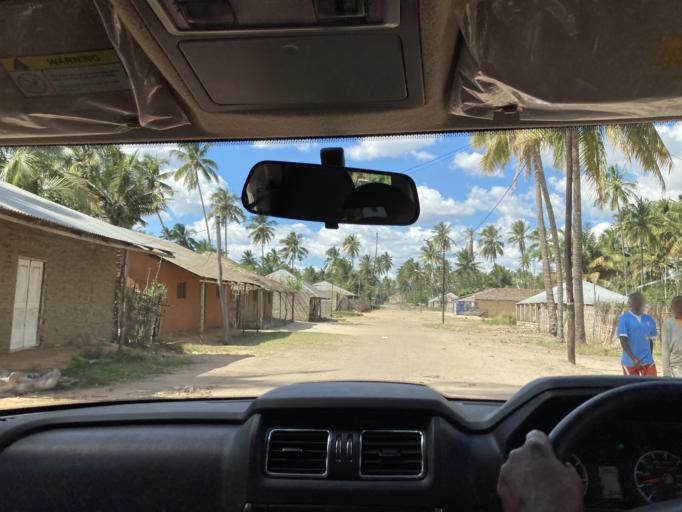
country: MZ
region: Cabo Delgado
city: Montepuez
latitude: -13.1307
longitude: 39.0067
